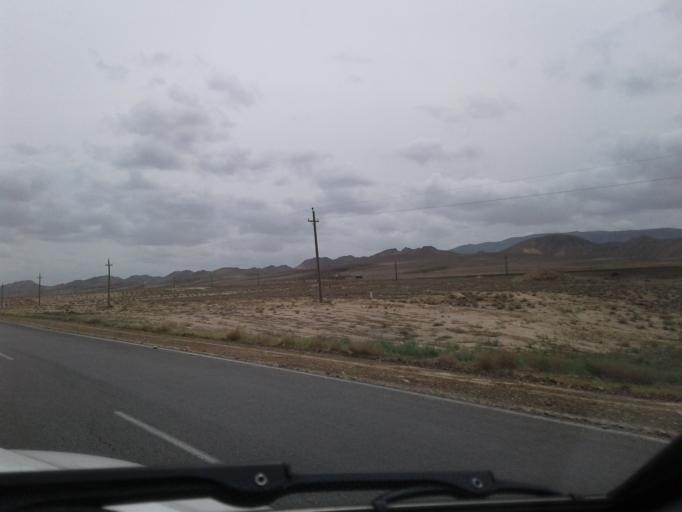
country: IR
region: Razavi Khorasan
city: Dargaz
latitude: 37.6365
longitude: 59.1494
